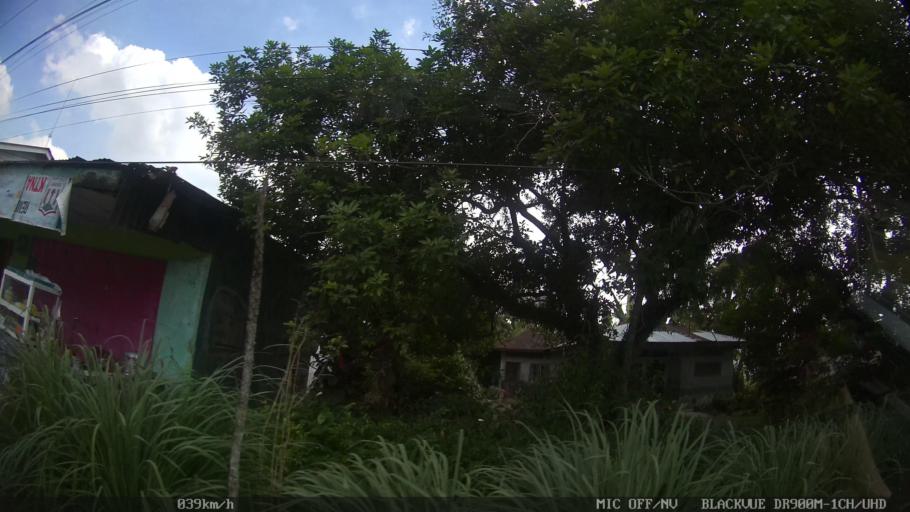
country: ID
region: North Sumatra
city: Binjai
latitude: 3.6353
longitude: 98.5069
